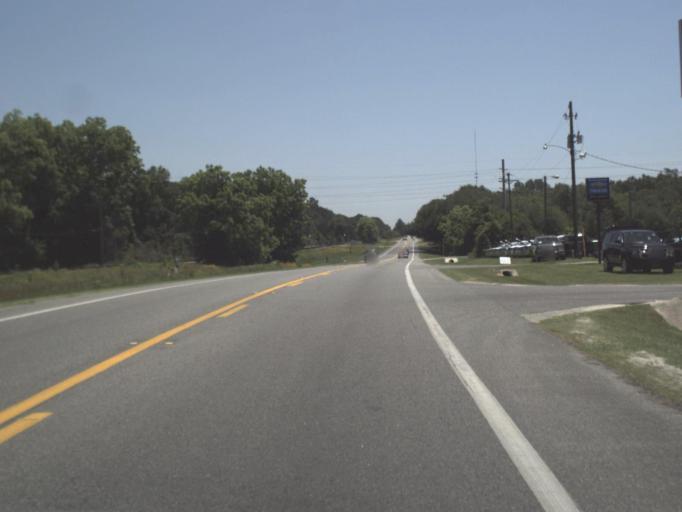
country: US
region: Florida
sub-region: Suwannee County
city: Live Oak
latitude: 30.2936
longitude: -82.9773
